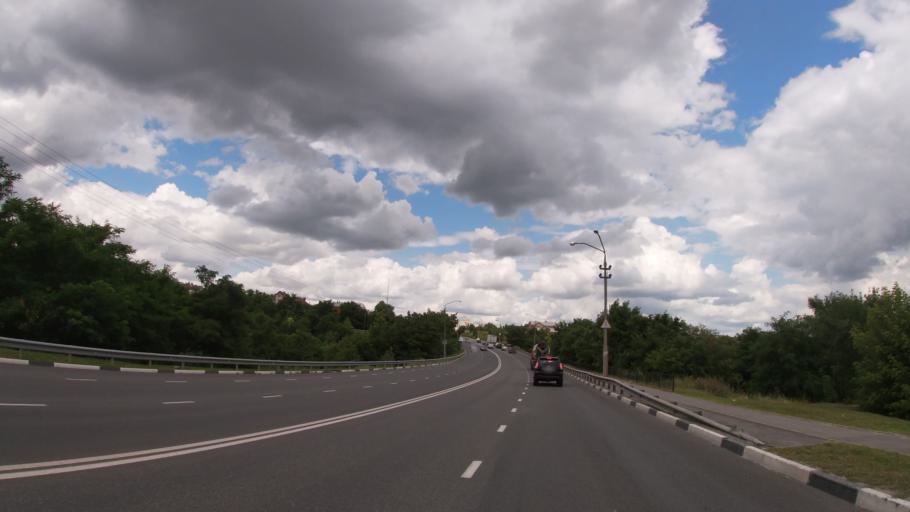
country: RU
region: Belgorod
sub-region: Belgorodskiy Rayon
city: Belgorod
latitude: 50.5586
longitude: 36.5863
